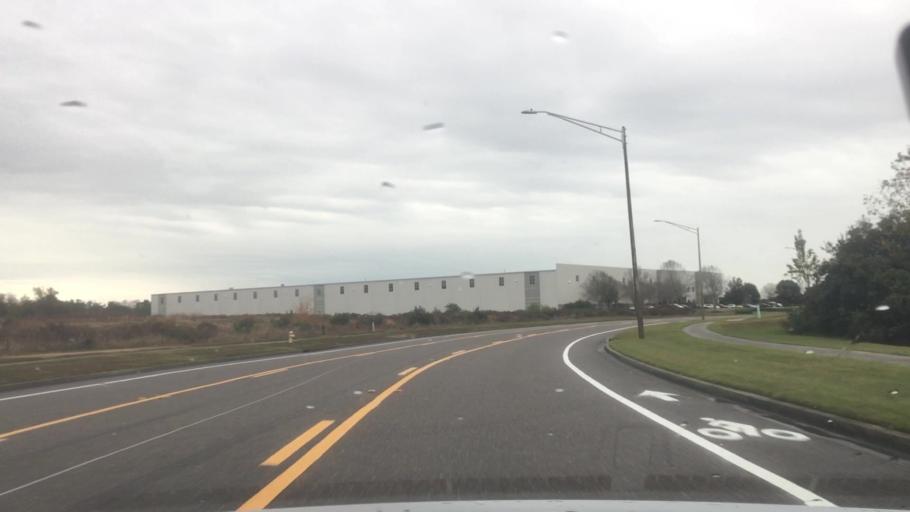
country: US
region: Florida
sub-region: Duval County
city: Jacksonville
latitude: 30.4505
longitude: -81.5725
